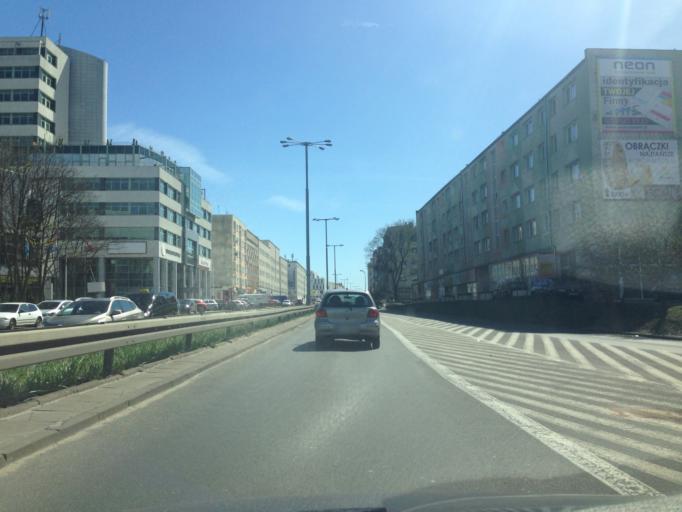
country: PL
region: Pomeranian Voivodeship
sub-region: Gdynia
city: Gdynia
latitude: 54.5171
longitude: 18.5315
